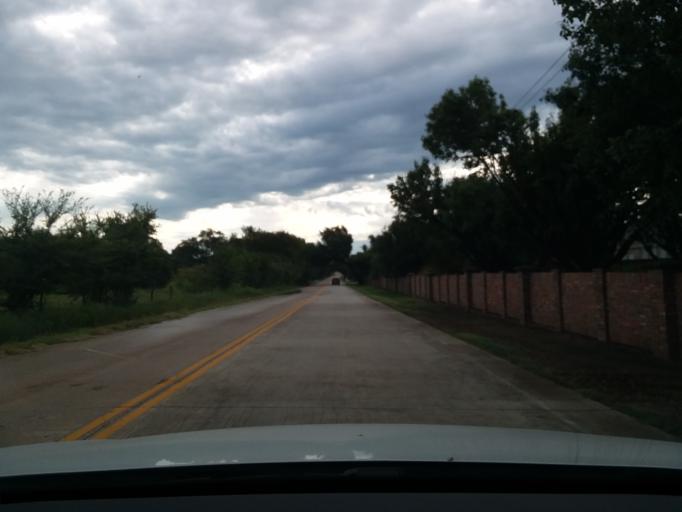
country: US
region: Texas
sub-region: Denton County
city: Double Oak
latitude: 33.0591
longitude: -97.0734
